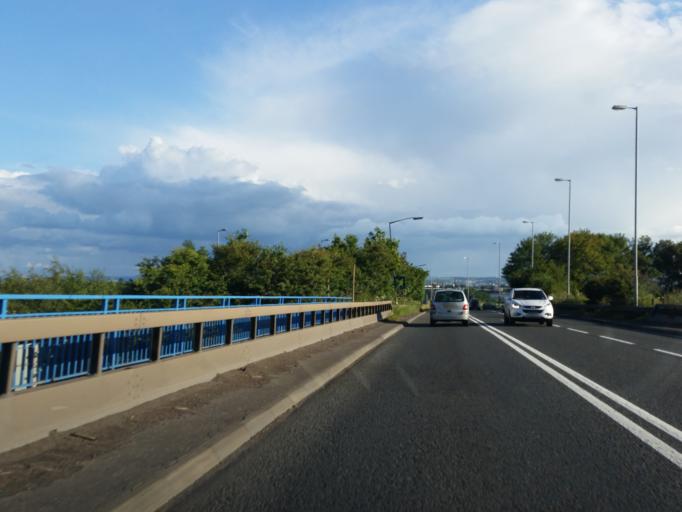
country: GB
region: Scotland
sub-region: North Lanarkshire
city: Coatbridge
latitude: 55.8413
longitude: -4.0243
